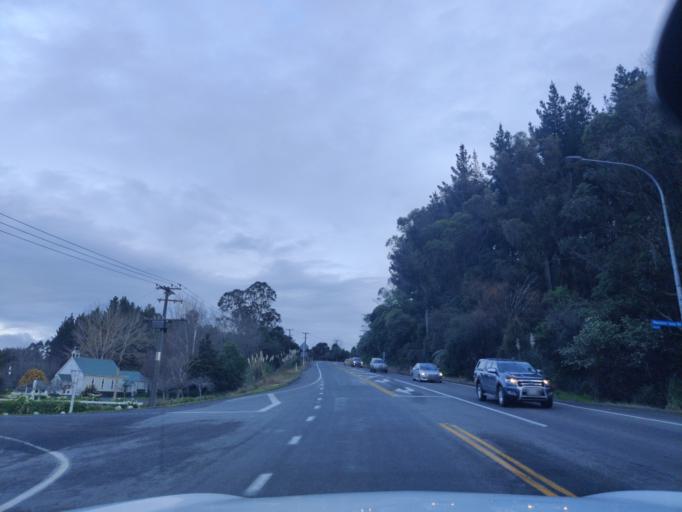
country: NZ
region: Manawatu-Wanganui
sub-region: Palmerston North City
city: Palmerston North
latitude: -40.3776
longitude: 175.6486
